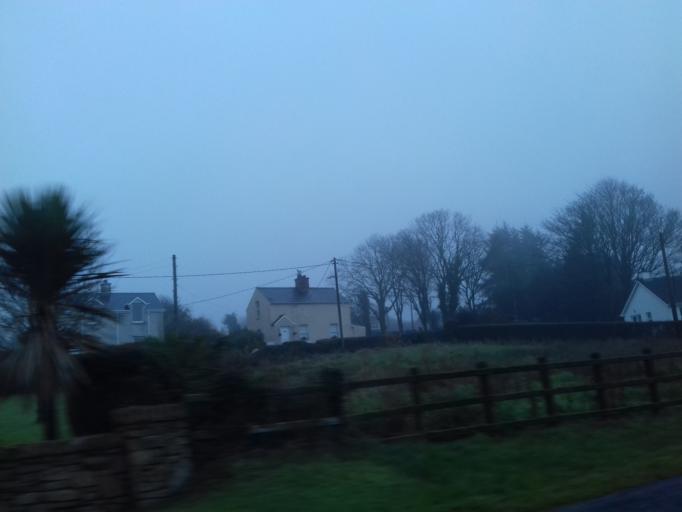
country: IE
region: Ulster
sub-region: County Donegal
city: Newtown Cunningham
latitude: 55.0917
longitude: -7.5512
